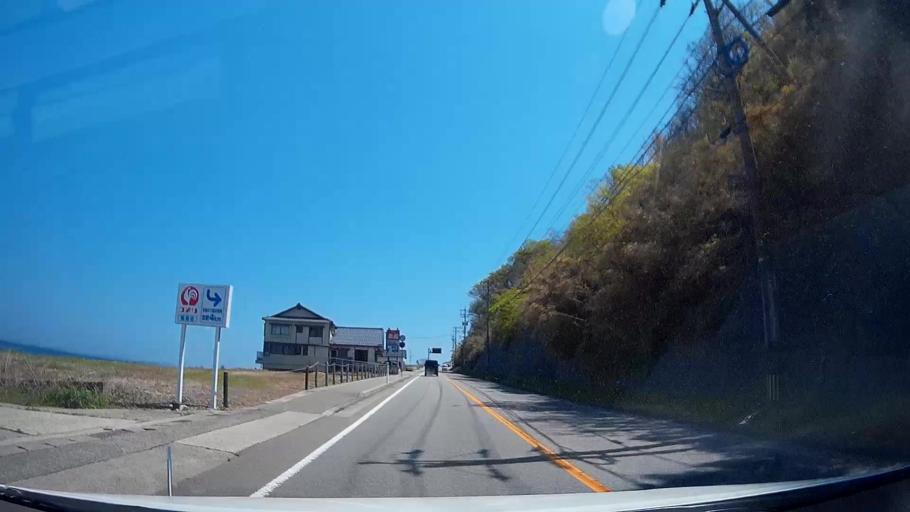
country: JP
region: Ishikawa
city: Nanao
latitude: 37.3959
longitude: 136.9285
